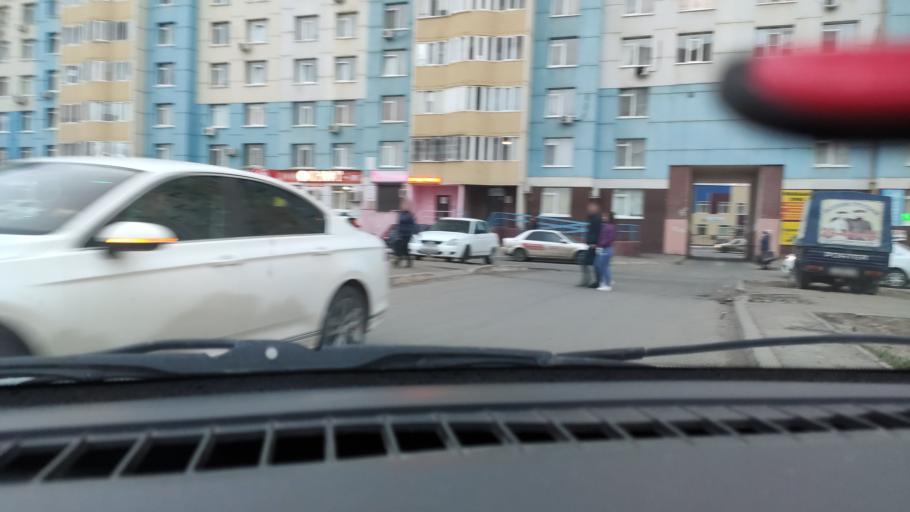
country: RU
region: Orenburg
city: Orenburg
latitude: 51.8123
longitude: 55.1773
